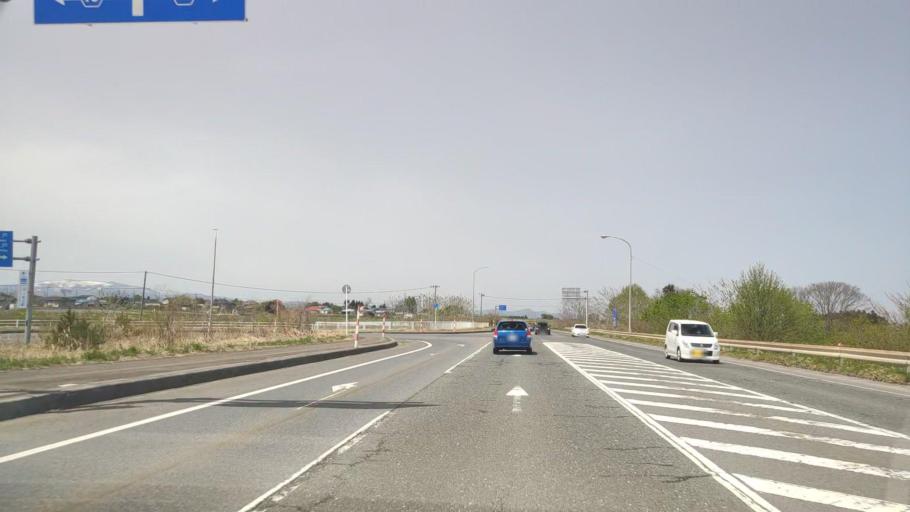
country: JP
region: Aomori
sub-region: Misawa Shi
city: Inuotose
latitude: 40.6328
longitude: 141.2462
